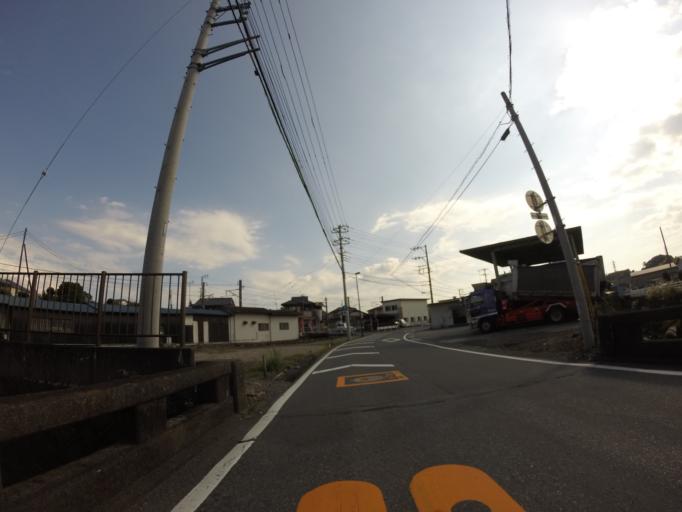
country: JP
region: Shizuoka
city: Fujinomiya
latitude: 35.1962
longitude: 138.6415
